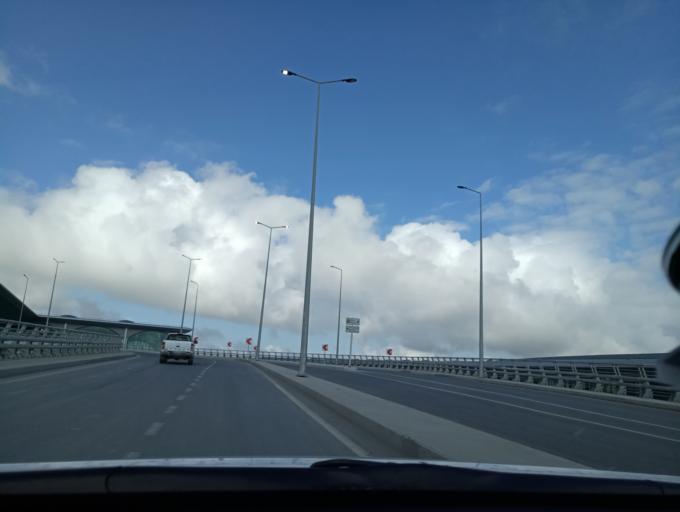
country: TR
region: Istanbul
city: Durusu
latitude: 41.2578
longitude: 28.7466
